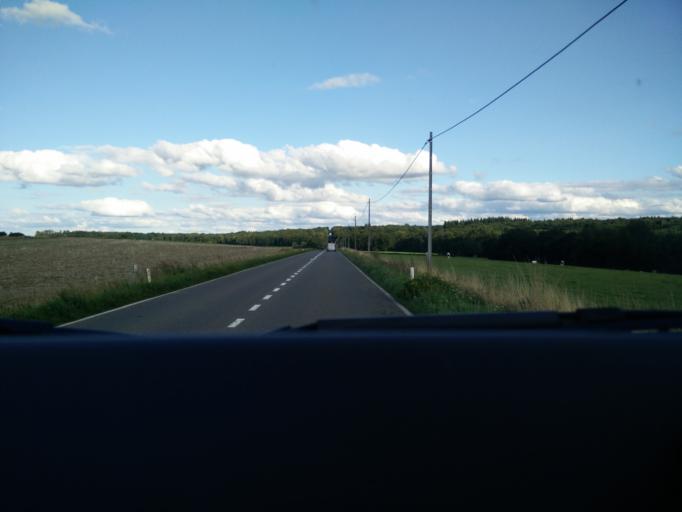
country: BE
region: Wallonia
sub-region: Province de Namur
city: Walcourt
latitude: 50.2097
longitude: 4.4673
